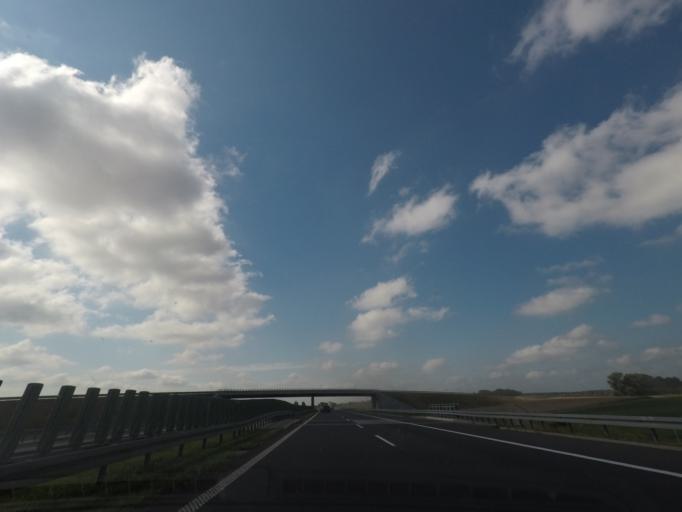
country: PL
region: Pomeranian Voivodeship
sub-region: Powiat starogardzki
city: Smetowo Graniczne
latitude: 53.7051
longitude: 18.6283
